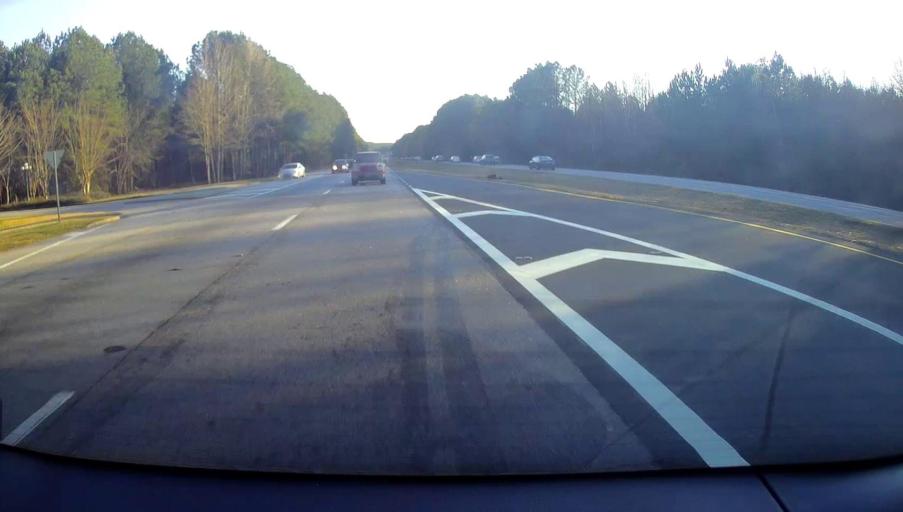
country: US
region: Georgia
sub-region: Fayette County
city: Tyrone
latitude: 33.4775
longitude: -84.5858
